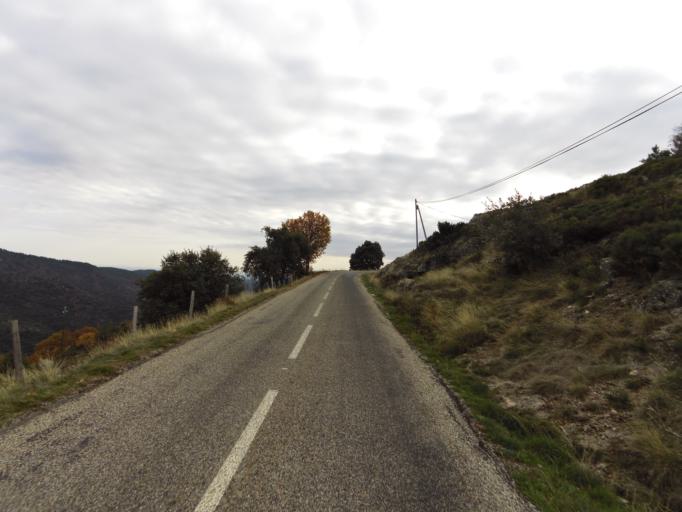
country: FR
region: Rhone-Alpes
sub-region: Departement de l'Ardeche
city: Les Vans
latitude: 44.5081
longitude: 4.0478
